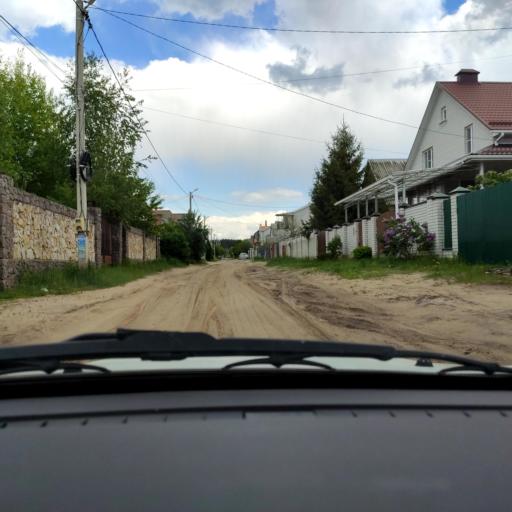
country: RU
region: Voronezj
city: Podgornoye
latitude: 51.7470
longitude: 39.1507
